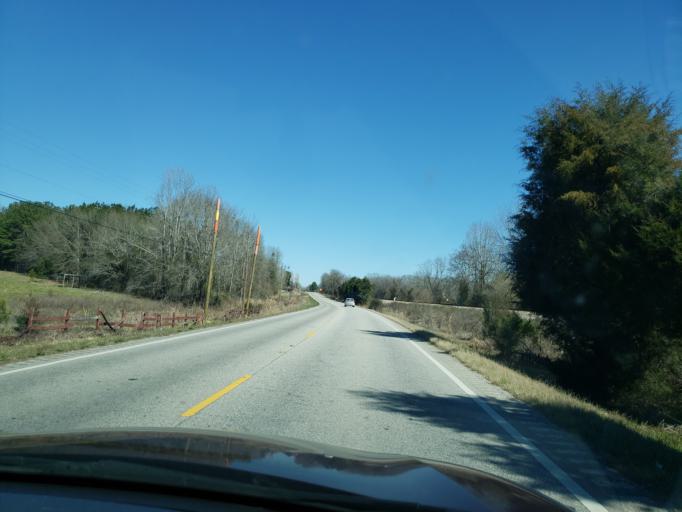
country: US
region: Alabama
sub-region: Lee County
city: Auburn
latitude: 32.5969
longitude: -85.6148
